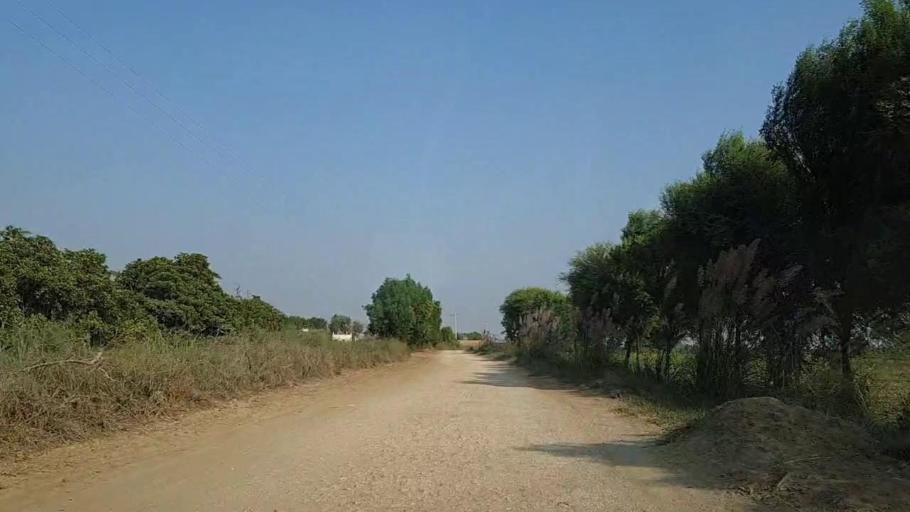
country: PK
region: Sindh
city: Mirpur Sakro
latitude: 24.6195
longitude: 67.6651
